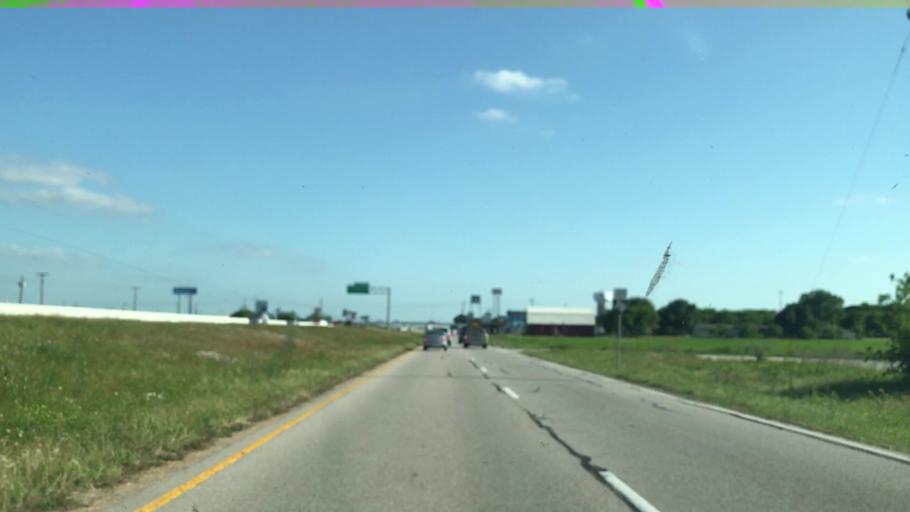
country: US
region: Texas
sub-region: Ellis County
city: Red Oak
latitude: 32.5366
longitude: -96.8225
